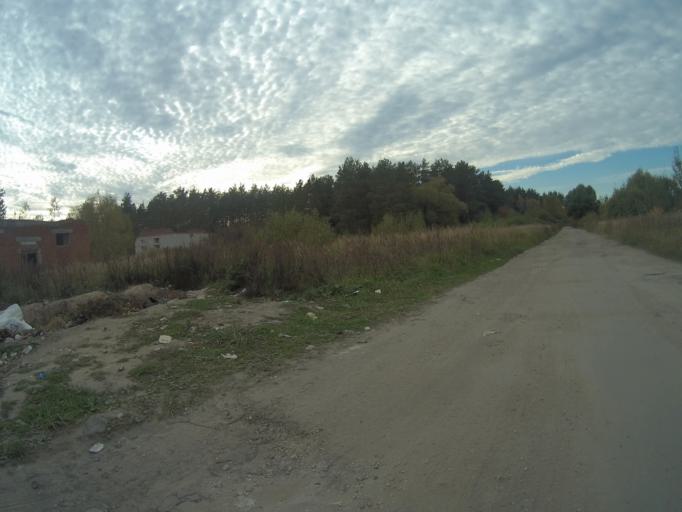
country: RU
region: Vladimir
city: Golovino
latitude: 55.9622
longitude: 40.4250
